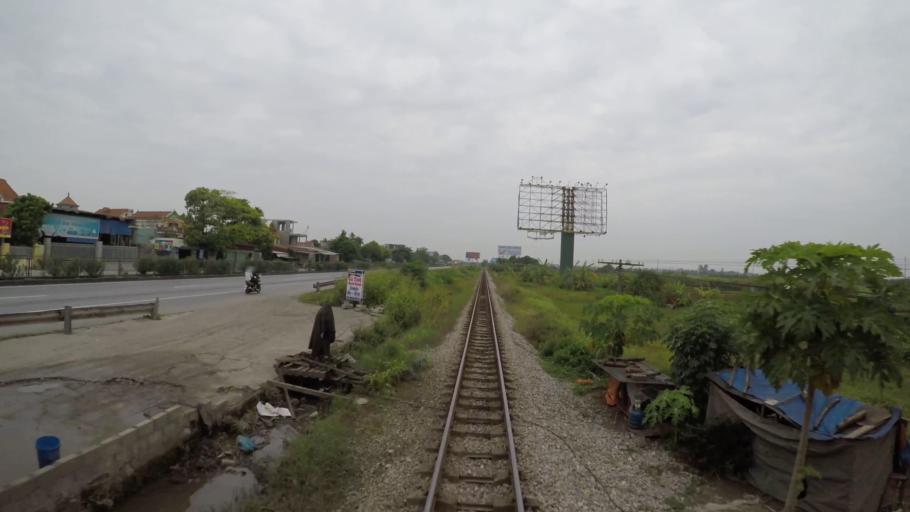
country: VN
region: Hai Duong
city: Phu Thai
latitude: 20.9370
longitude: 106.5489
